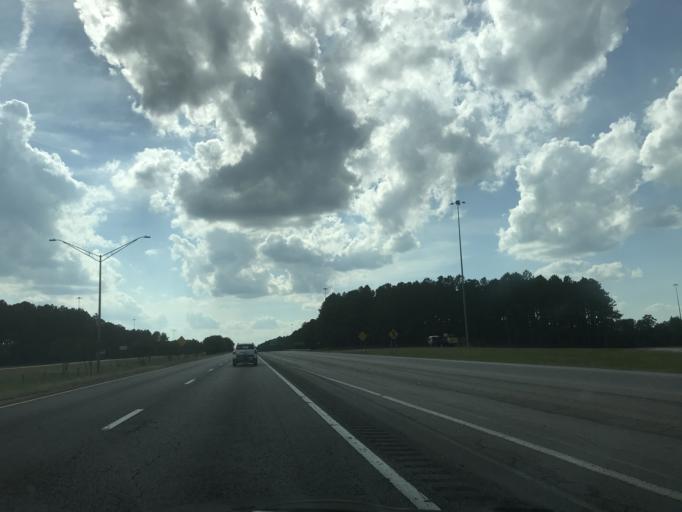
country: US
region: North Carolina
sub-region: Nash County
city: Red Oak
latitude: 35.9817
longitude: -77.8729
